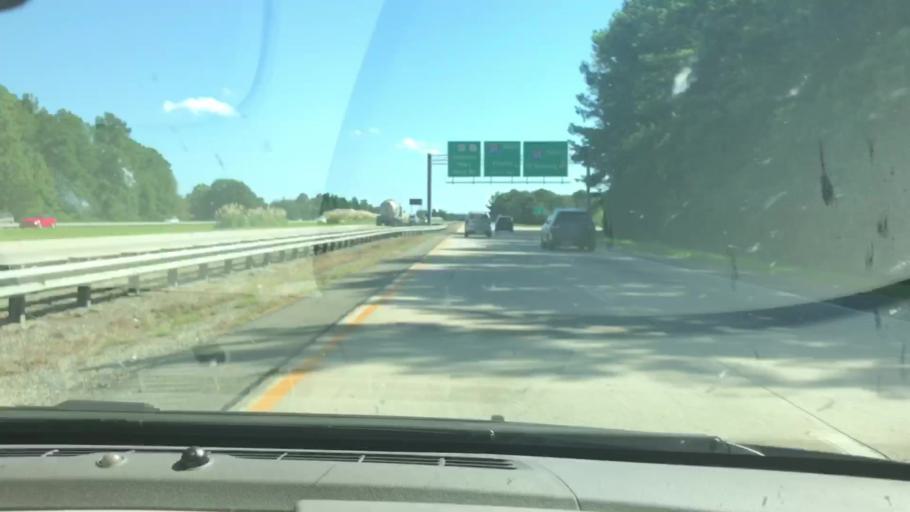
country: US
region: Alabama
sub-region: Russell County
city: Phenix City
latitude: 32.5420
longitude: -84.9667
